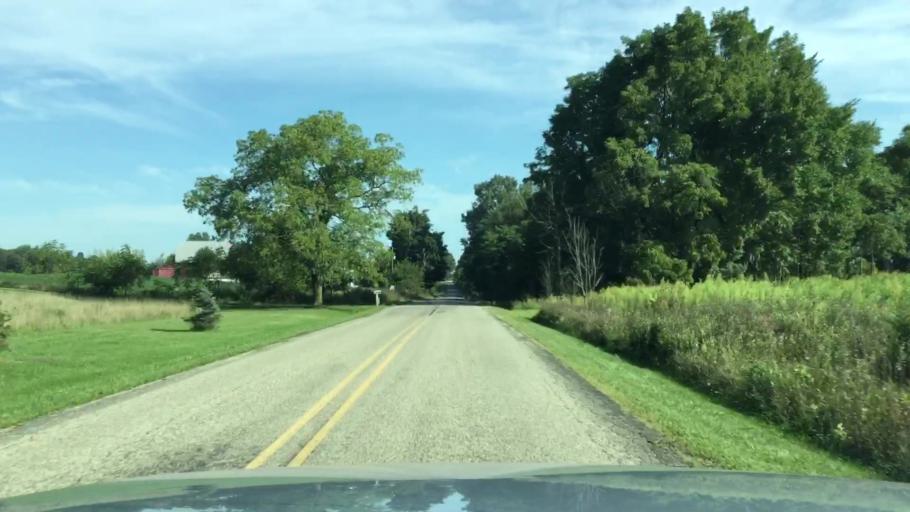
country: US
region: Michigan
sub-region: Lenawee County
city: Hudson
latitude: 41.8905
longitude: -84.4203
